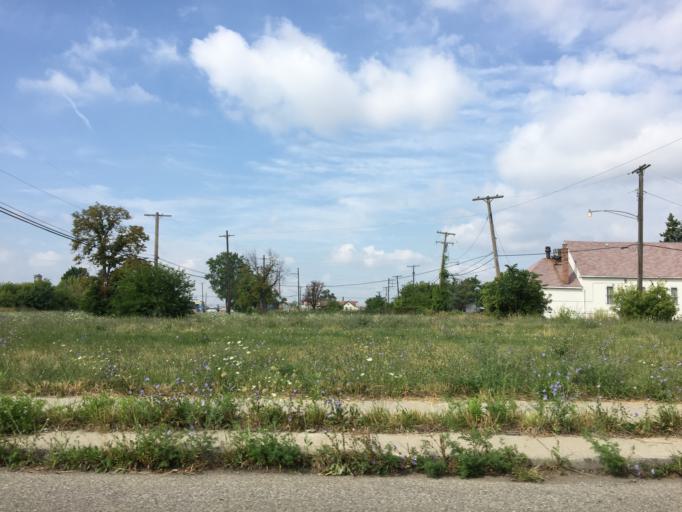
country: US
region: Michigan
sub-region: Wayne County
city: Detroit
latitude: 42.3547
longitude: -83.0336
